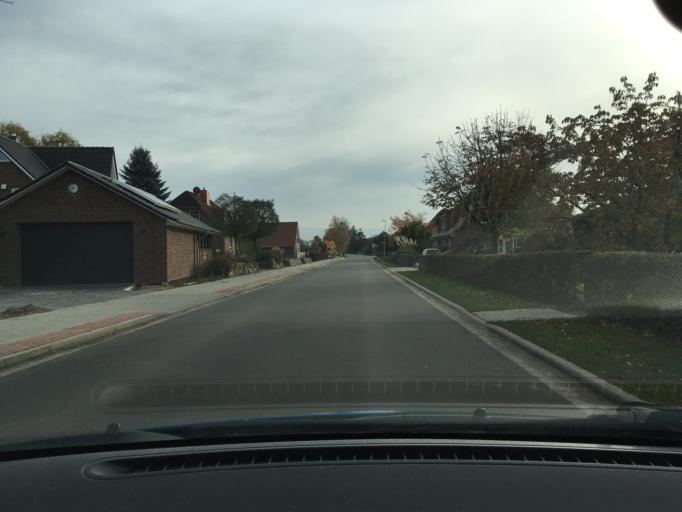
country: DE
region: Lower Saxony
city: Wittorf
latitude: 53.3270
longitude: 10.3822
